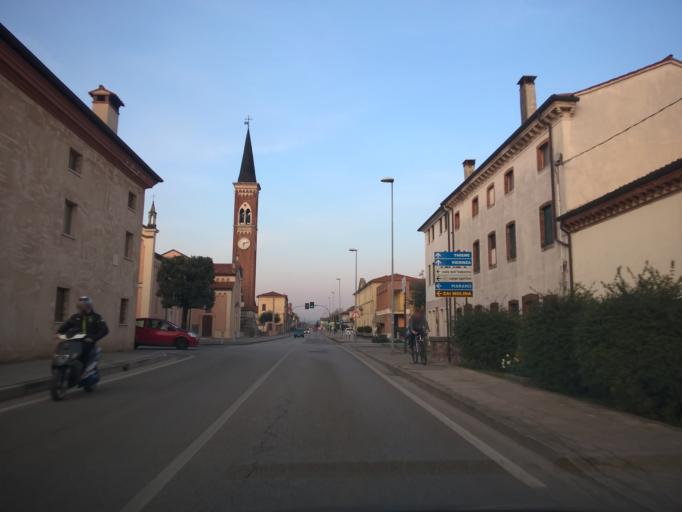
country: IT
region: Veneto
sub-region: Provincia di Vicenza
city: Villaverla
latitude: 45.6709
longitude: 11.4626
